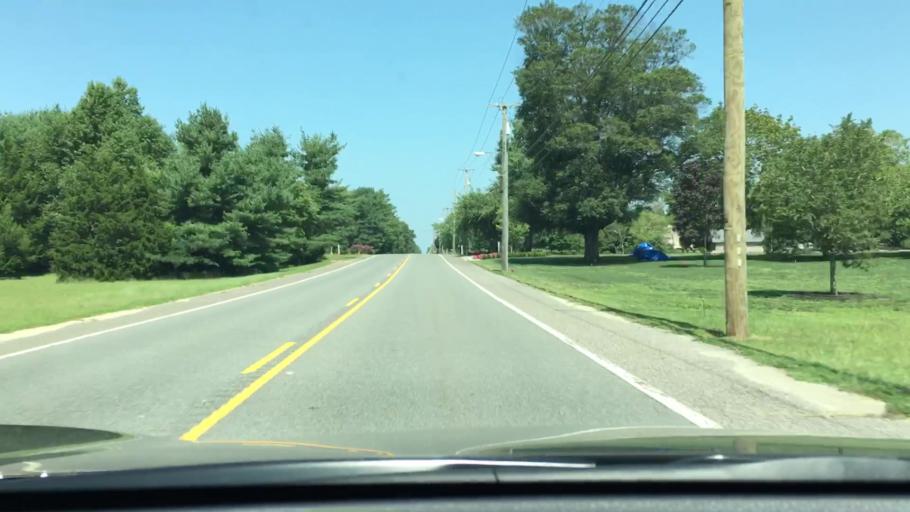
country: US
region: New Jersey
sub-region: Cumberland County
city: Laurel Lake
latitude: 39.2924
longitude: -74.9969
